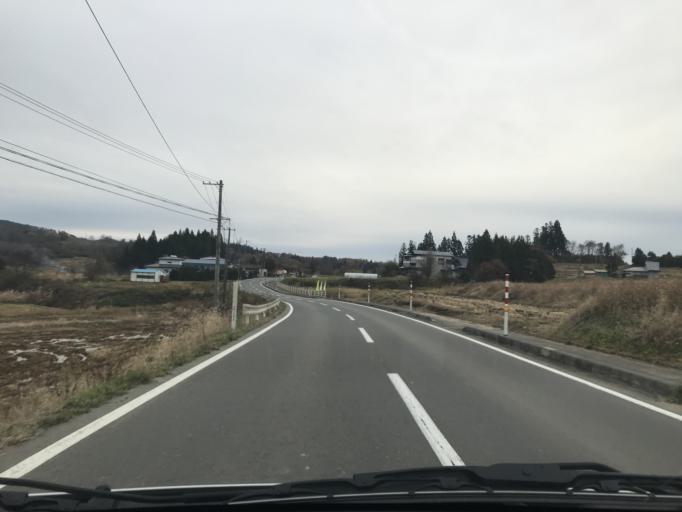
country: JP
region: Iwate
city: Kitakami
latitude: 39.2756
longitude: 141.2668
